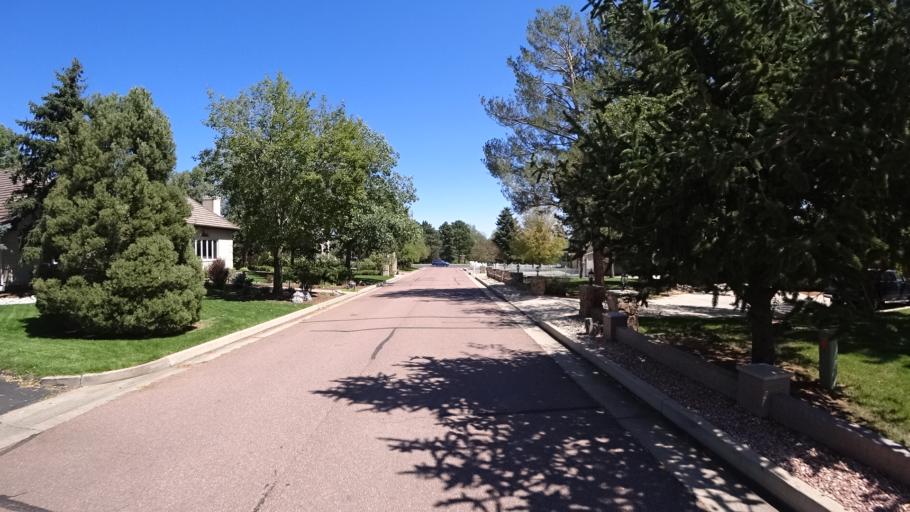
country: US
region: Colorado
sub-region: El Paso County
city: Colorado Springs
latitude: 38.7936
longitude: -104.8344
